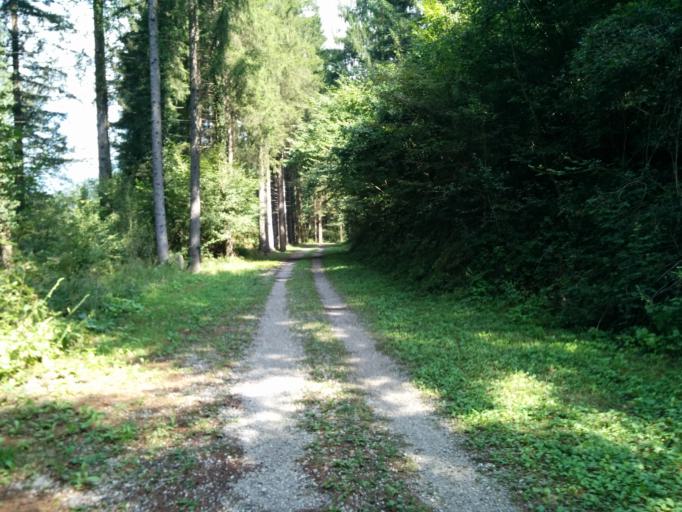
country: IT
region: Friuli Venezia Giulia
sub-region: Provincia di Udine
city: Ovaro
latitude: 46.4627
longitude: 12.8728
